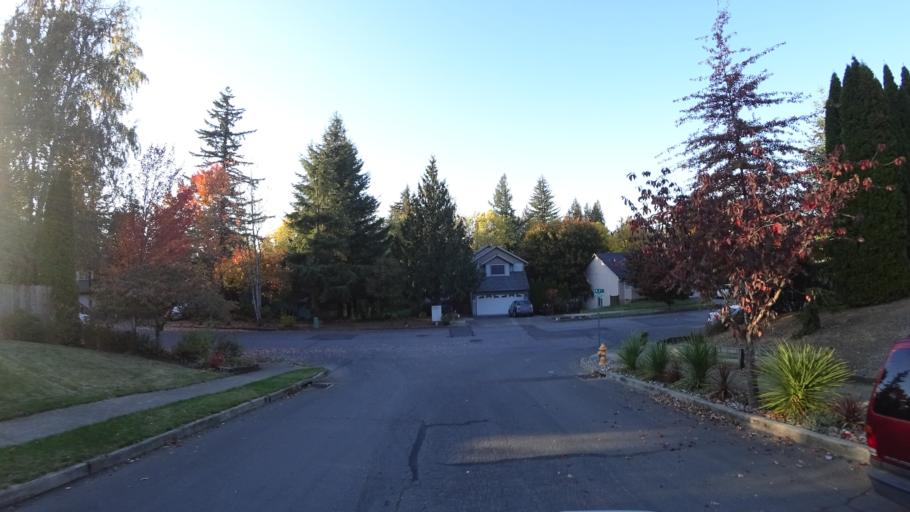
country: US
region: Oregon
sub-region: Multnomah County
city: Gresham
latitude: 45.4921
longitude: -122.4427
